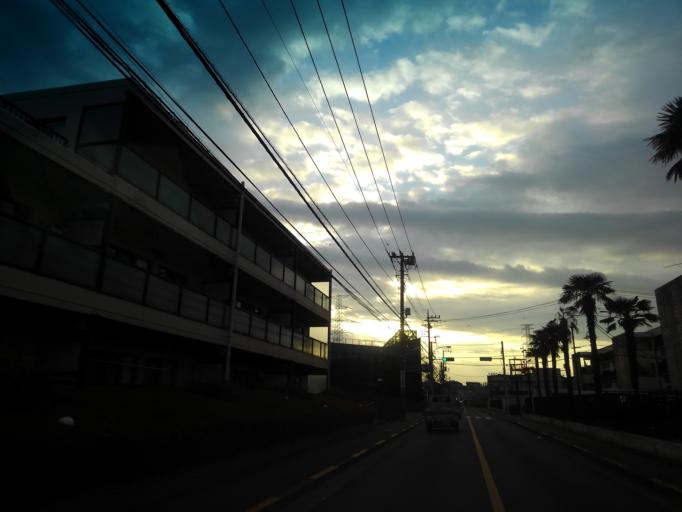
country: JP
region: Tokyo
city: Kokubunji
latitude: 35.7013
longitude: 139.4572
